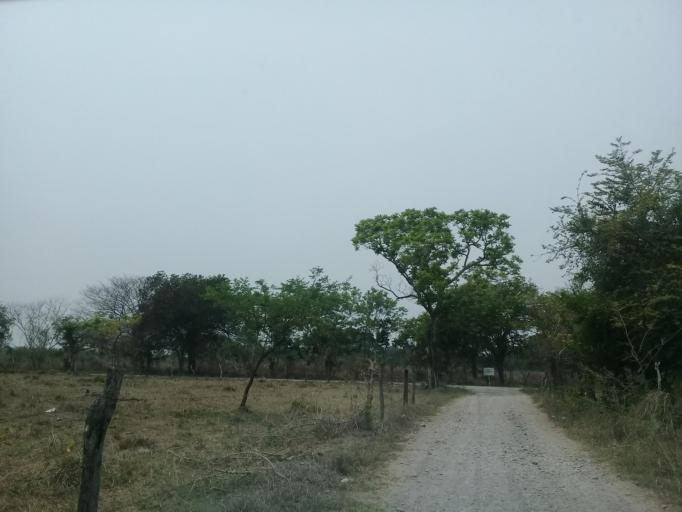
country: MX
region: Veracruz
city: Jamapa
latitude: 18.9332
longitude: -96.2055
